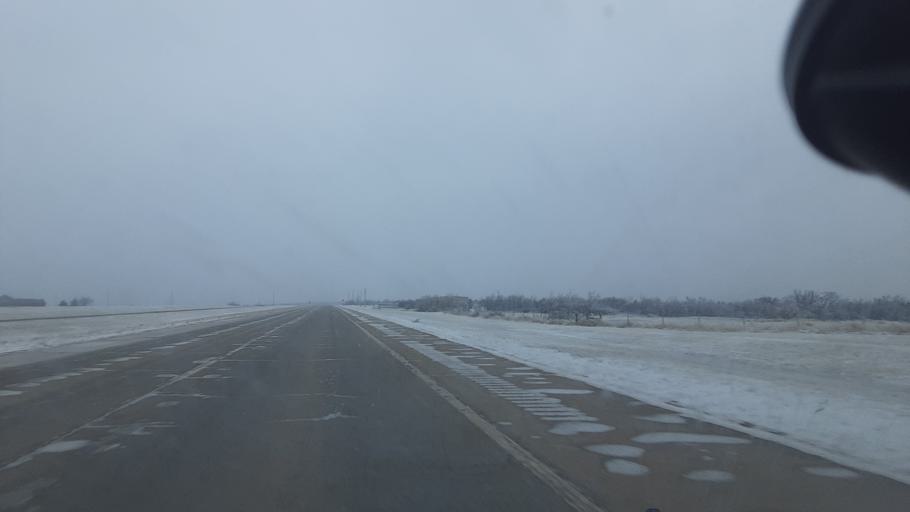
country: US
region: Oklahoma
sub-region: Logan County
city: Langston
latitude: 35.9176
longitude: -97.3279
